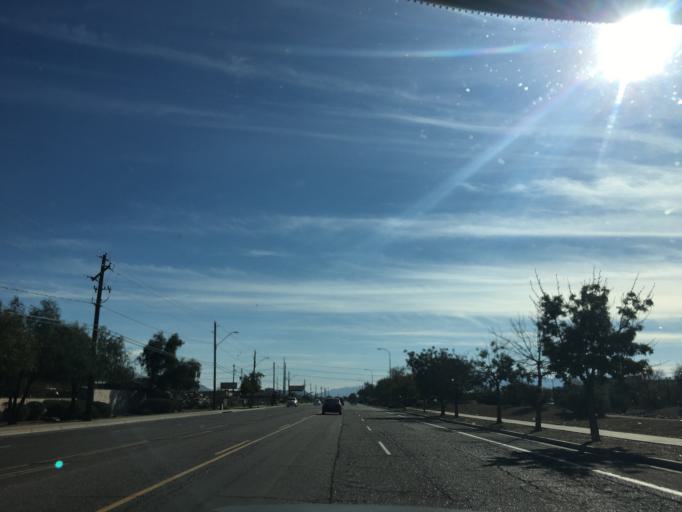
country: US
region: Arizona
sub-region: Maricopa County
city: Laveen
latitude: 33.4204
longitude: -112.1694
